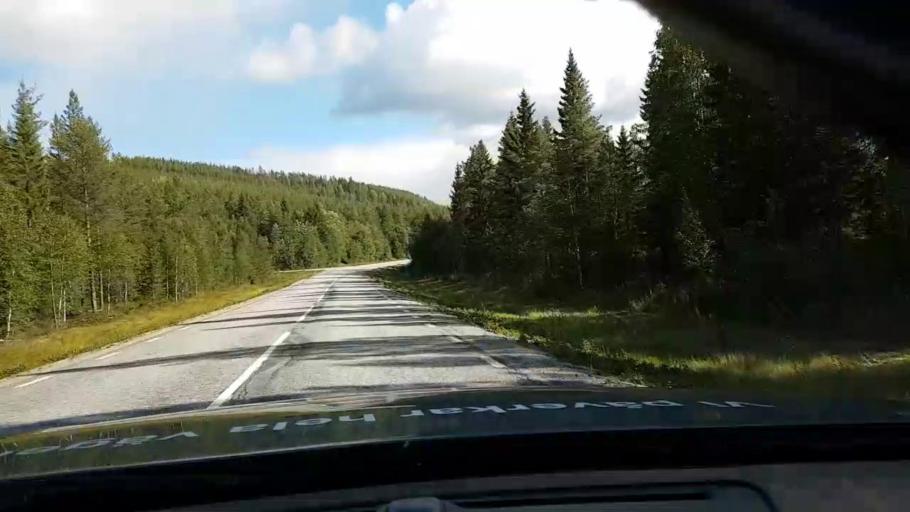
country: SE
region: Vaesternorrland
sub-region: OErnskoeldsviks Kommun
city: Bredbyn
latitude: 63.7588
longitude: 17.6977
